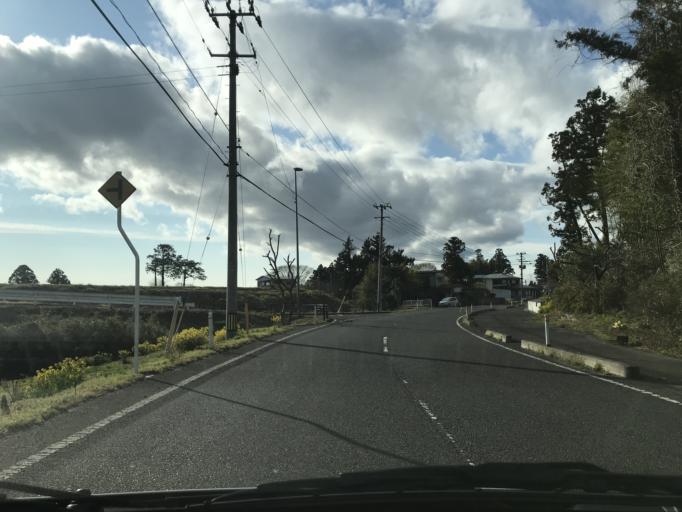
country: JP
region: Miyagi
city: Wakuya
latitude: 38.6216
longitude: 141.2266
